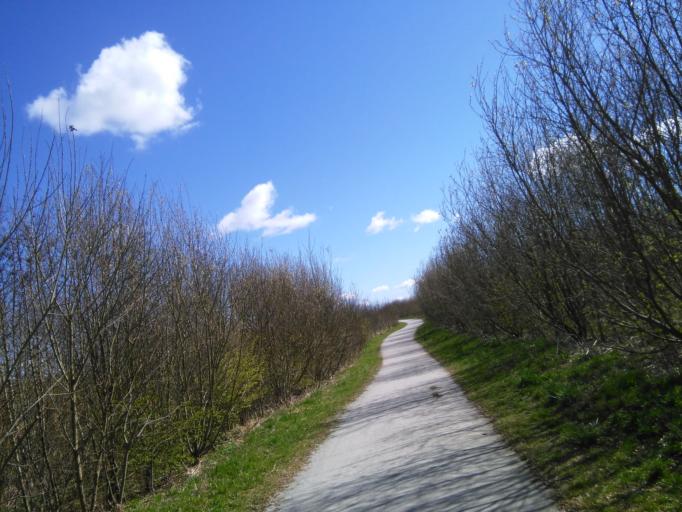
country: DK
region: Central Jutland
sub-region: Arhus Kommune
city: Lystrup
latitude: 56.2126
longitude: 10.2217
